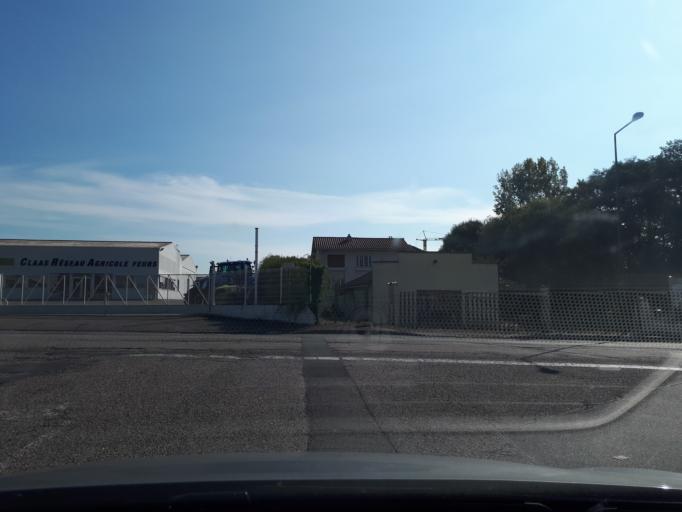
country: FR
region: Rhone-Alpes
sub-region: Departement de la Loire
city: Feurs
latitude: 45.7347
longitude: 4.2283
